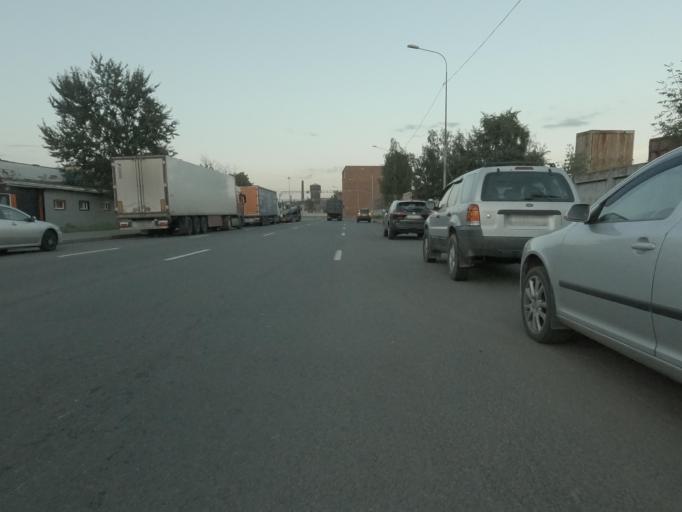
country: RU
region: St.-Petersburg
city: Vasyl'evsky Ostrov
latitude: 59.9036
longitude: 30.2420
